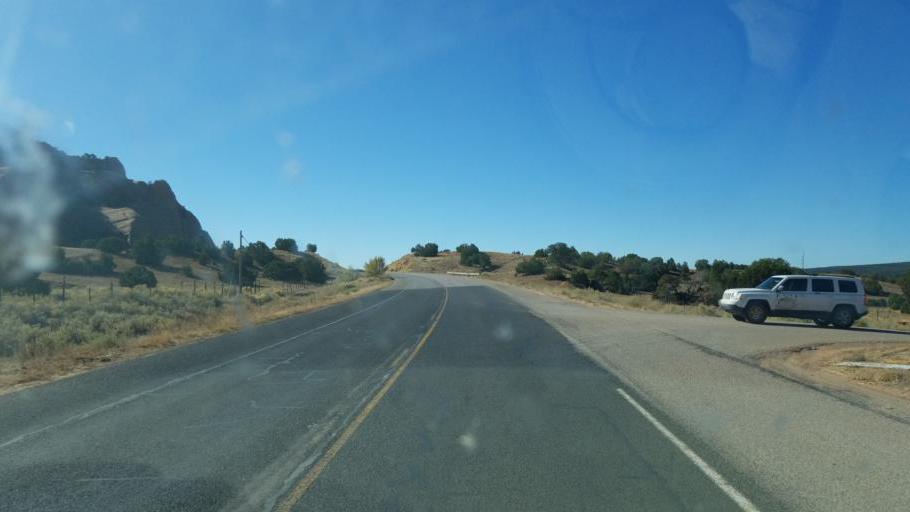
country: US
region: Arizona
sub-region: Apache County
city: Fort Defiance
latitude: 35.8105
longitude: -109.0374
